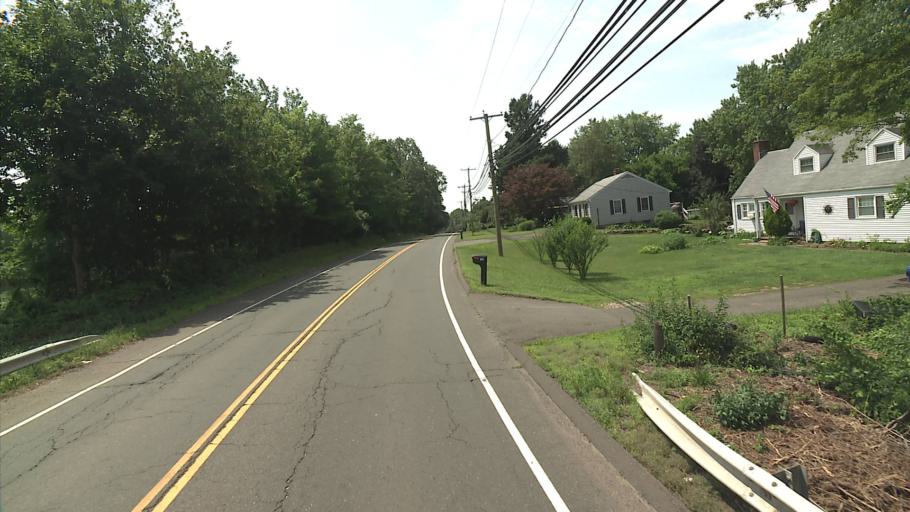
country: US
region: Connecticut
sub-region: New Haven County
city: North Branford
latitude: 41.3149
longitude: -72.7704
